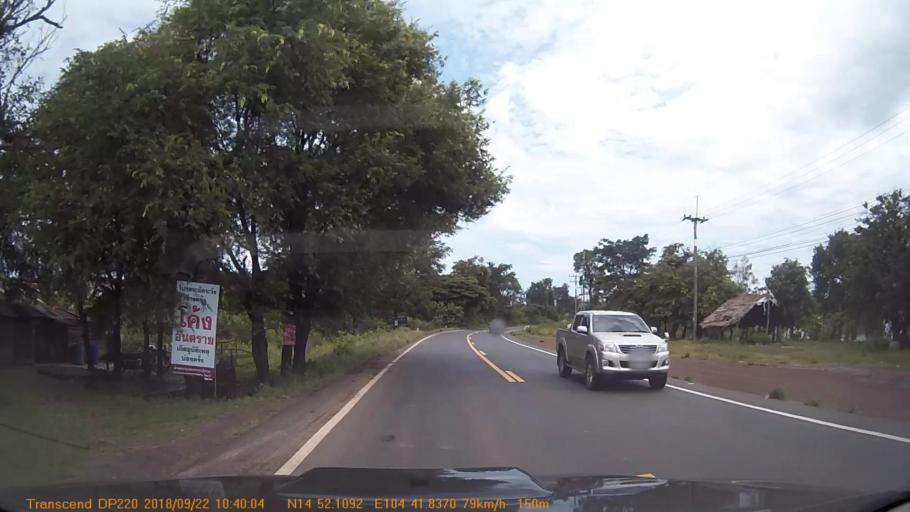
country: TH
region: Sisaket
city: Non Kho
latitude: 14.8686
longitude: 104.6973
